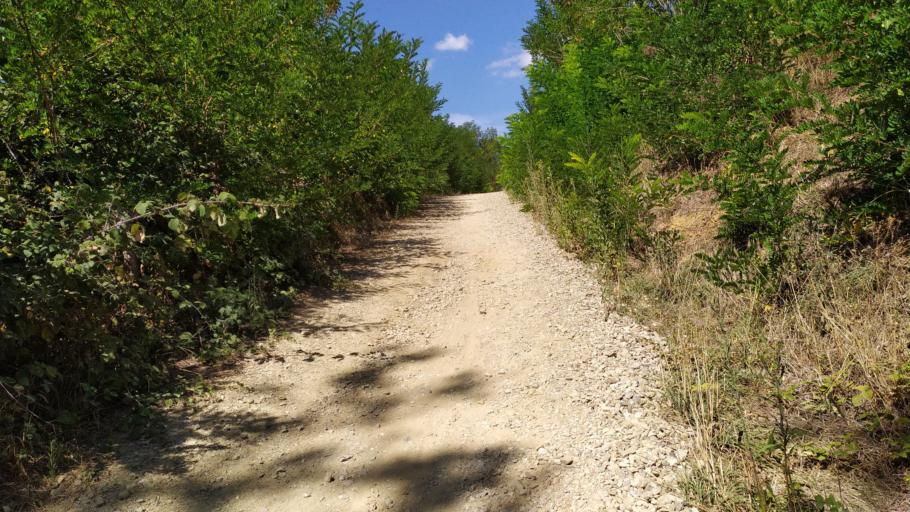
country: IT
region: Emilia-Romagna
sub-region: Forli-Cesena
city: Castrocaro Terme e Terra del Sole
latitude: 44.2044
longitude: 12.0041
